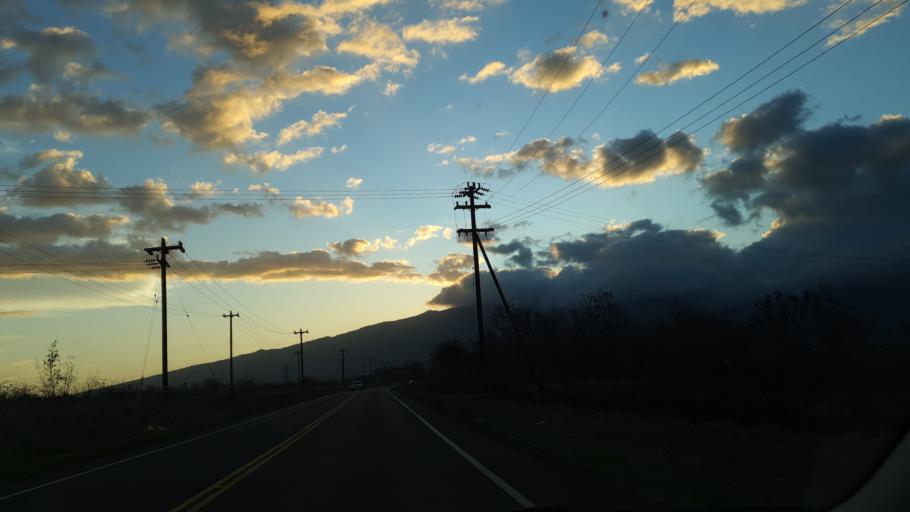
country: US
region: Hawaii
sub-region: Maui County
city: Kahului
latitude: 20.8723
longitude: -156.4403
